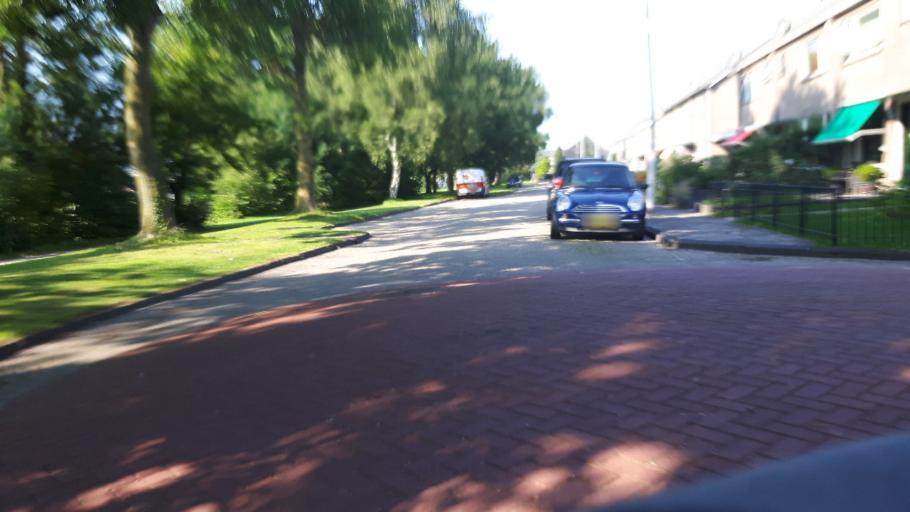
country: NL
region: Friesland
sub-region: Gemeente Franekeradeel
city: Franeker
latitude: 53.1887
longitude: 5.5552
